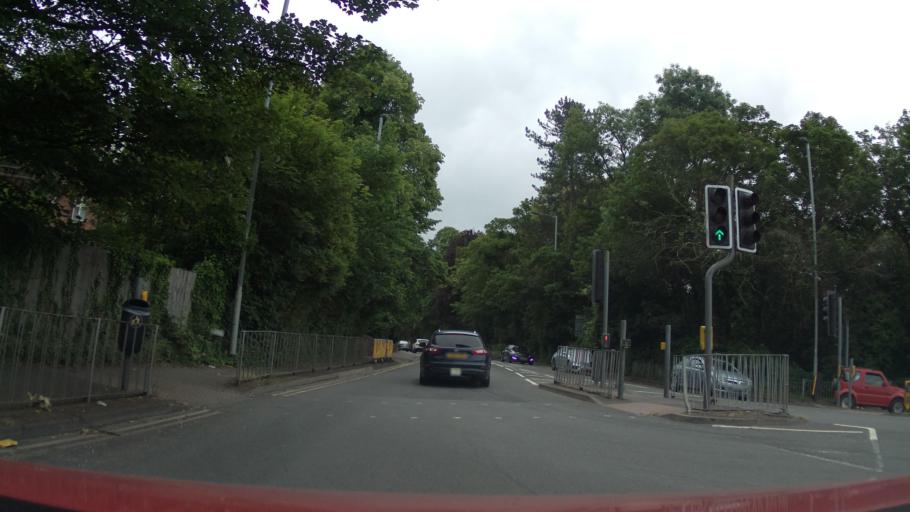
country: GB
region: England
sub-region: Staffordshire
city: Burton upon Trent
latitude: 52.8058
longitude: -1.6191
